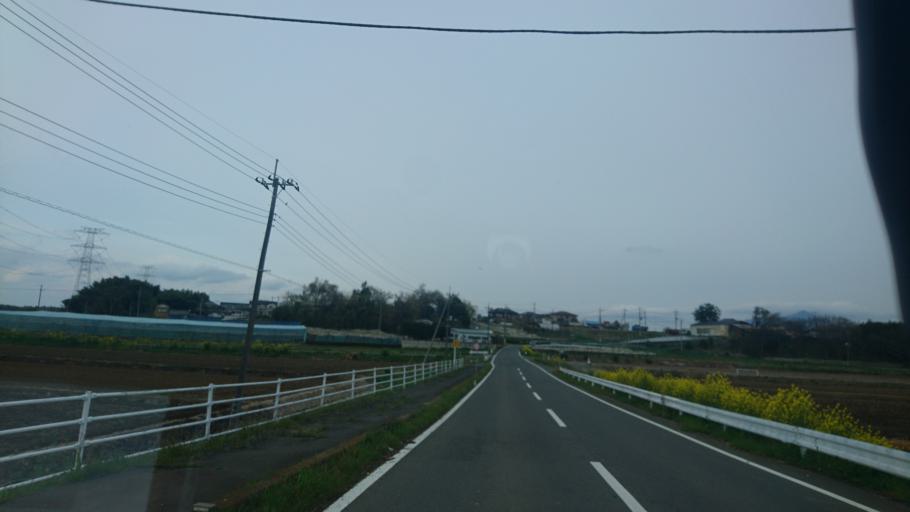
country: JP
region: Ibaraki
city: Shimodate
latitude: 36.2181
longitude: 139.9649
